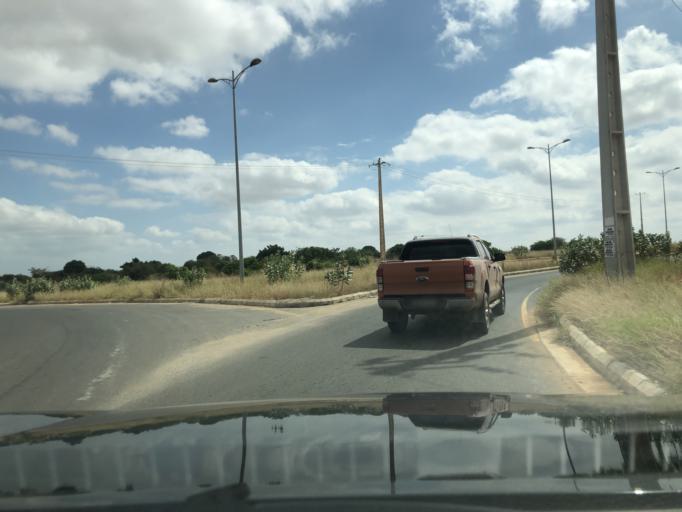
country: AO
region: Luanda
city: Luanda
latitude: -8.9583
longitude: 13.2392
